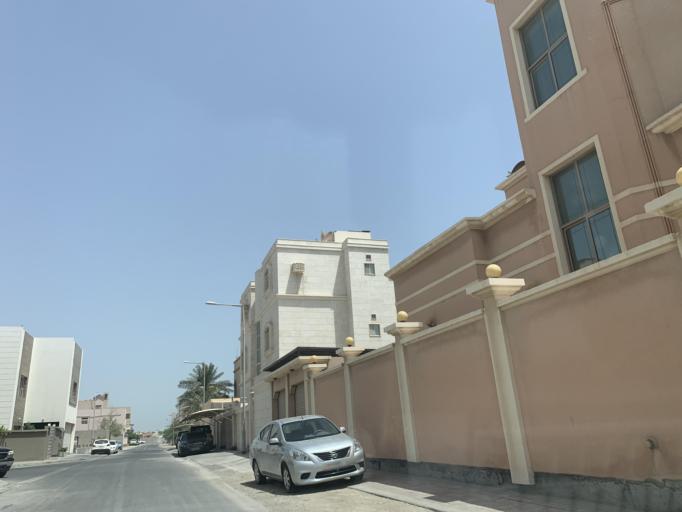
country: BH
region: Northern
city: Ar Rifa'
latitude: 26.1564
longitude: 50.5802
